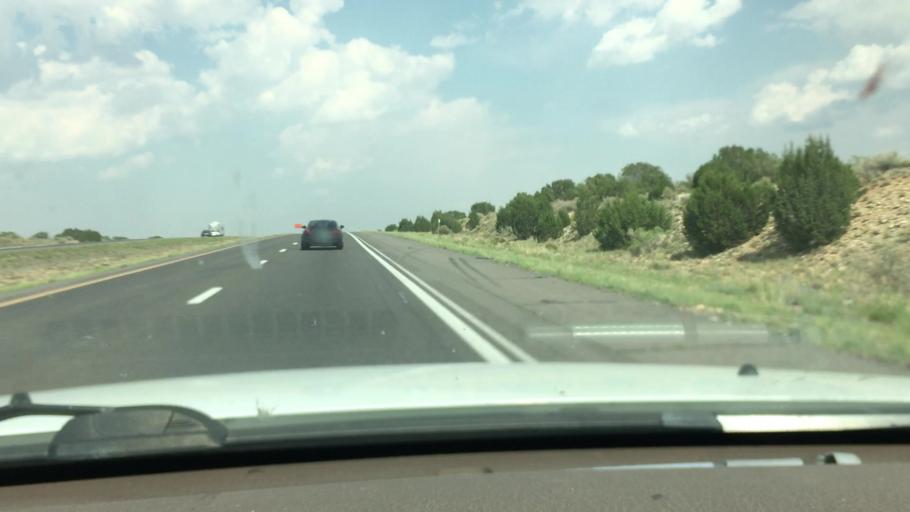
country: US
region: New Mexico
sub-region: Cibola County
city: Skyline-Ganipa
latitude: 35.0756
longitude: -107.6352
